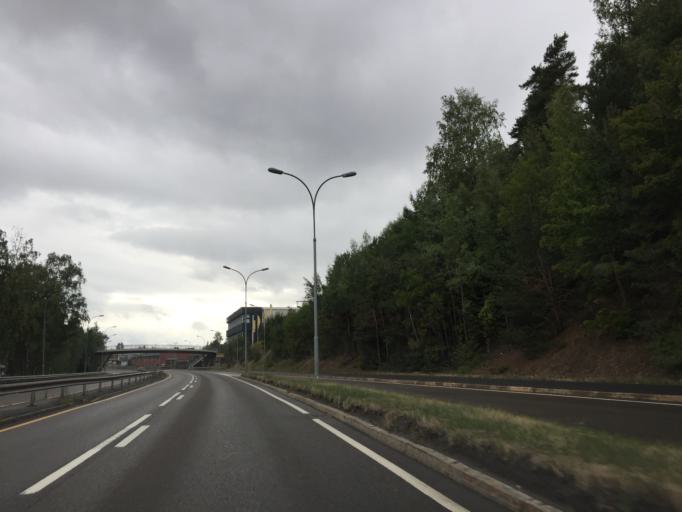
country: NO
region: Oslo
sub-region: Oslo
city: Oslo
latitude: 59.9375
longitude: 10.8360
